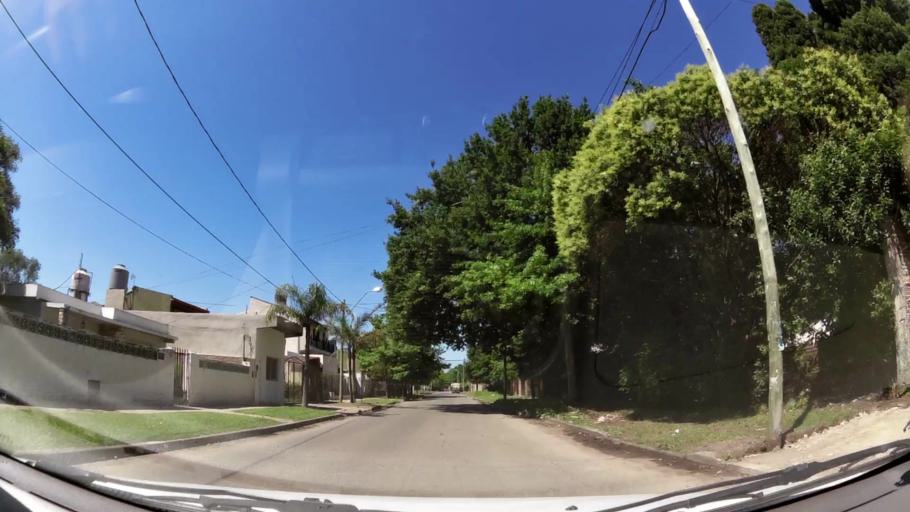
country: AR
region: Buenos Aires
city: Ituzaingo
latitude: -34.6816
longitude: -58.6587
